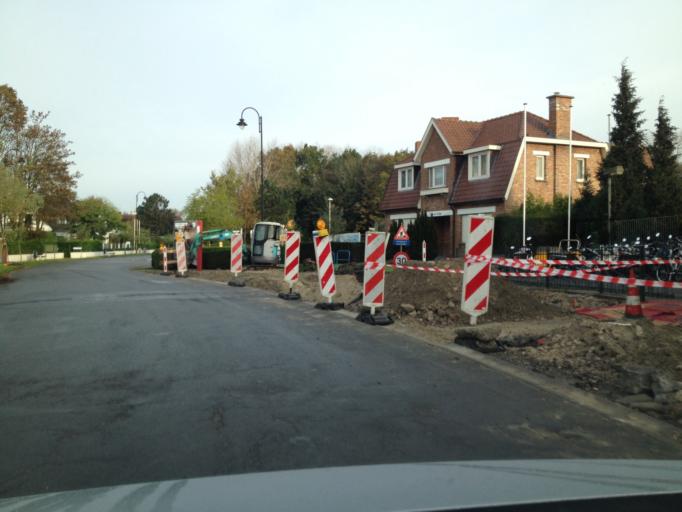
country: BE
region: Flanders
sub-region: Provincie West-Vlaanderen
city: Knokke-Heist
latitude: 51.3504
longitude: 3.3268
